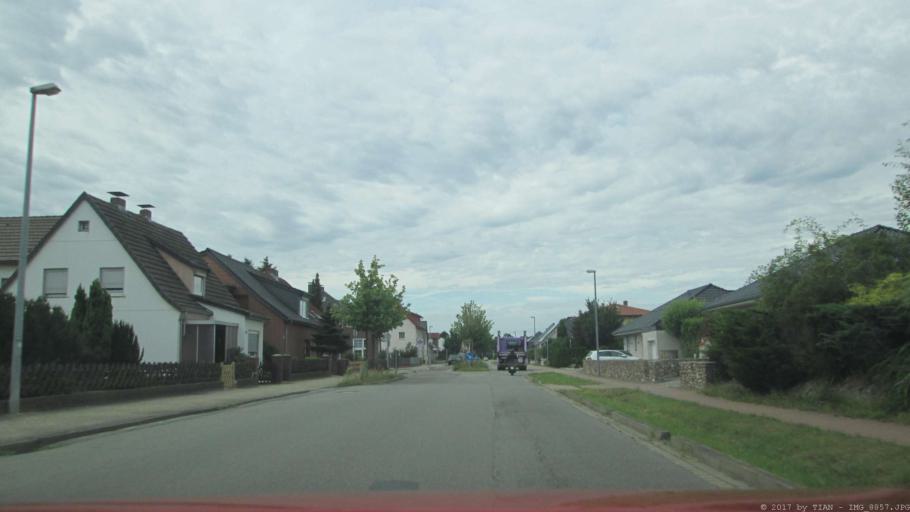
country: DE
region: Lower Saxony
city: Wolfsburg
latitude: 52.4471
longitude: 10.7765
